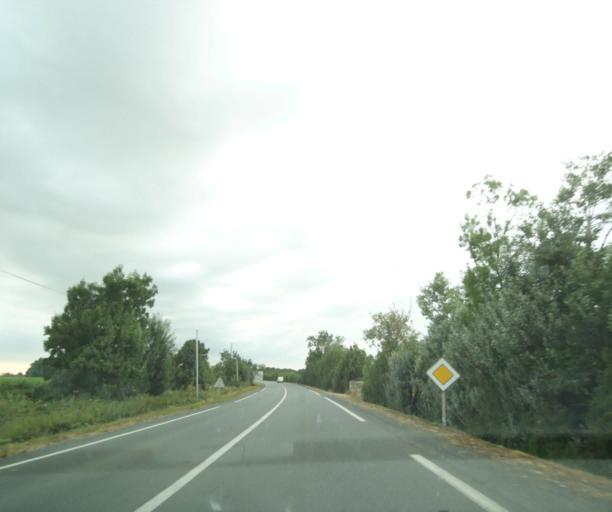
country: FR
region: Pays de la Loire
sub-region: Departement de la Vendee
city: Chaille-les-Marais
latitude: 46.4097
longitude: -1.0378
